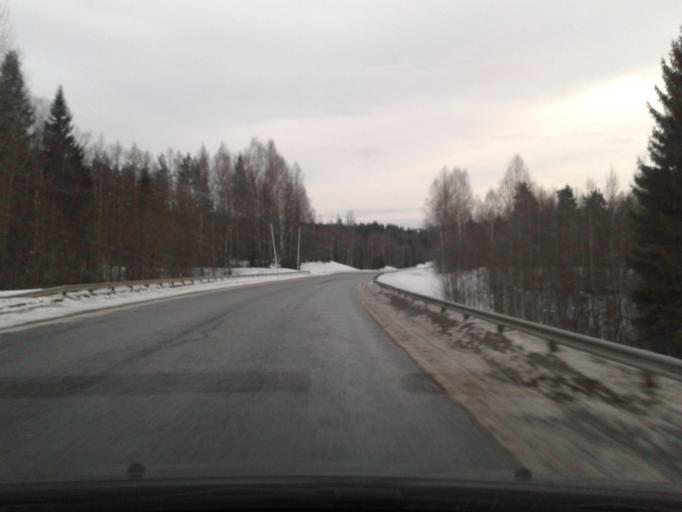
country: SE
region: Vaesternorrland
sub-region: Solleftea Kommun
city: Solleftea
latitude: 63.2865
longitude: 17.2231
